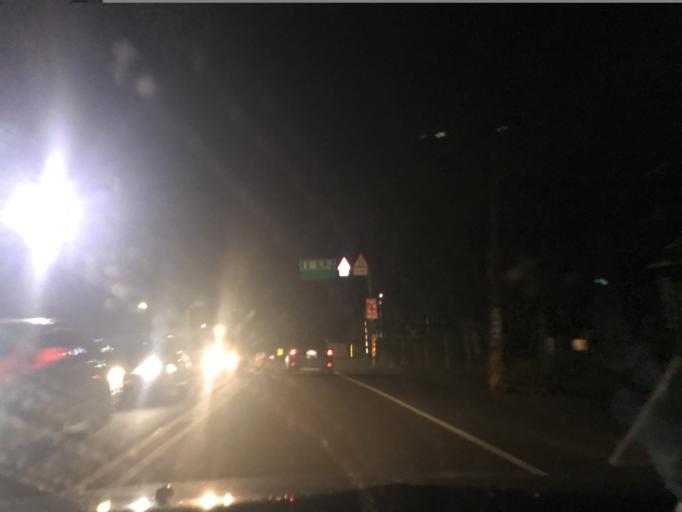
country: TW
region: Taiwan
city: Daxi
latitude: 24.9336
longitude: 121.2617
